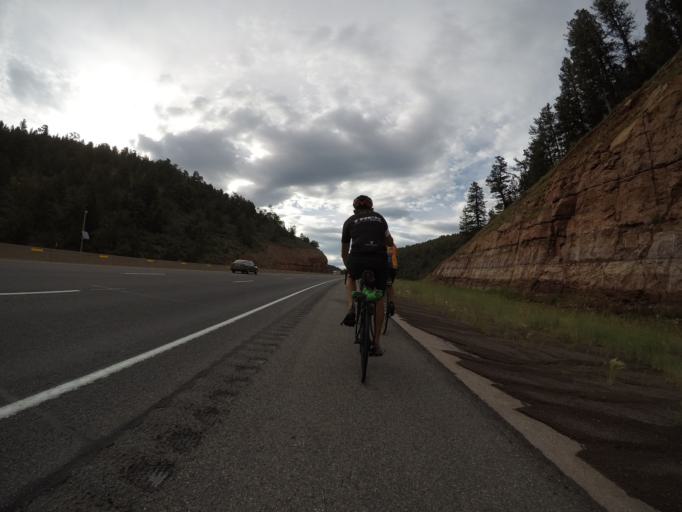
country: US
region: Wyoming
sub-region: Albany County
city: Laramie
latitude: 41.2648
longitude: -105.4672
